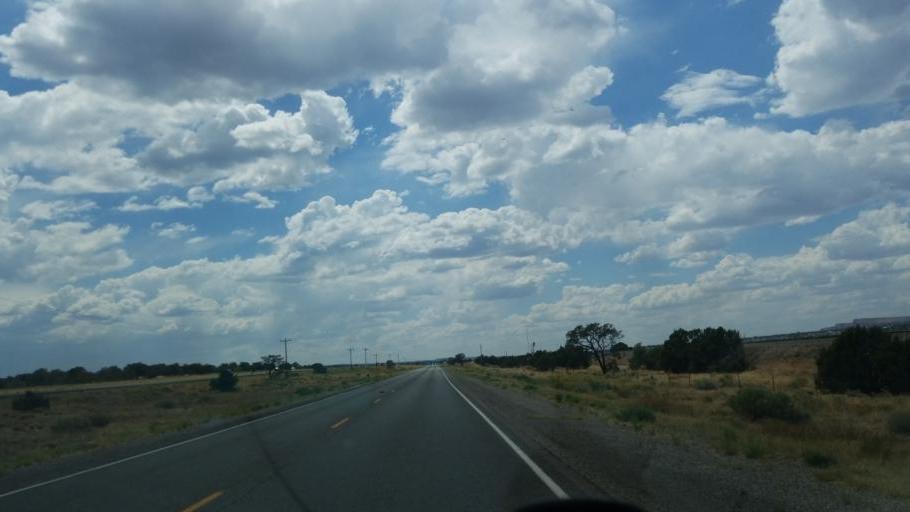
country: US
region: New Mexico
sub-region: McKinley County
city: Thoreau
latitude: 35.3894
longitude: -108.1724
